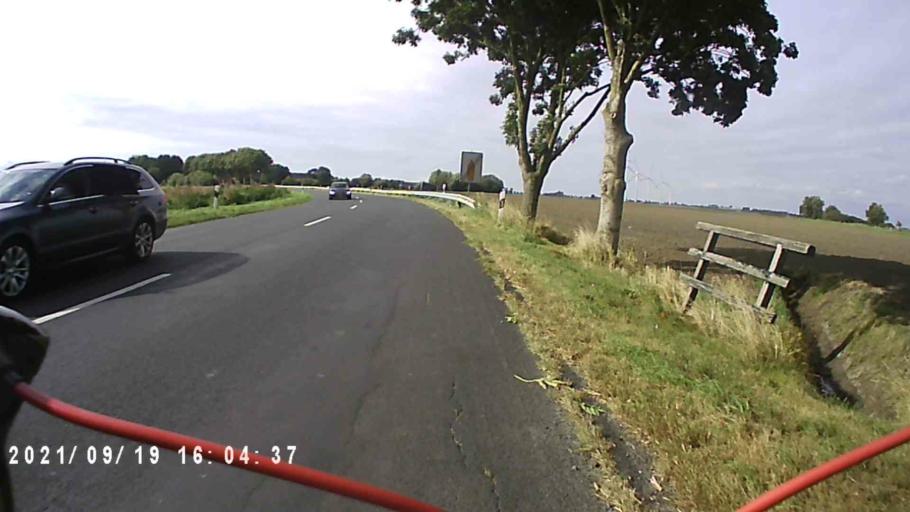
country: DE
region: Lower Saxony
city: Bunde
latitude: 53.1852
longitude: 7.2531
